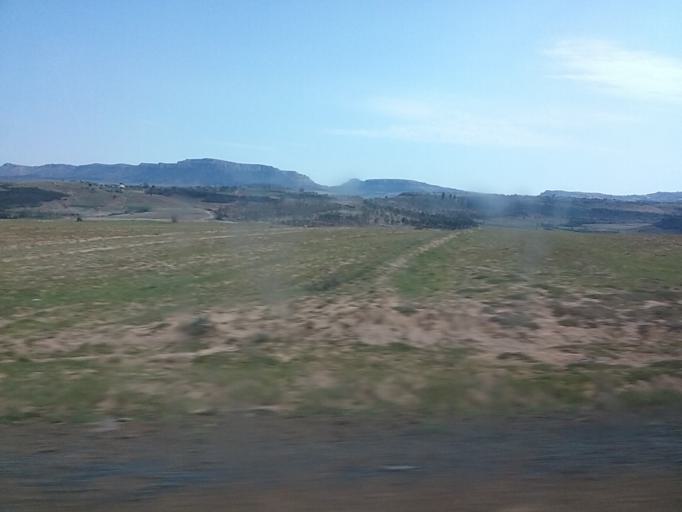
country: LS
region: Berea
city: Teyateyaneng
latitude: -29.0849
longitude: 27.9203
